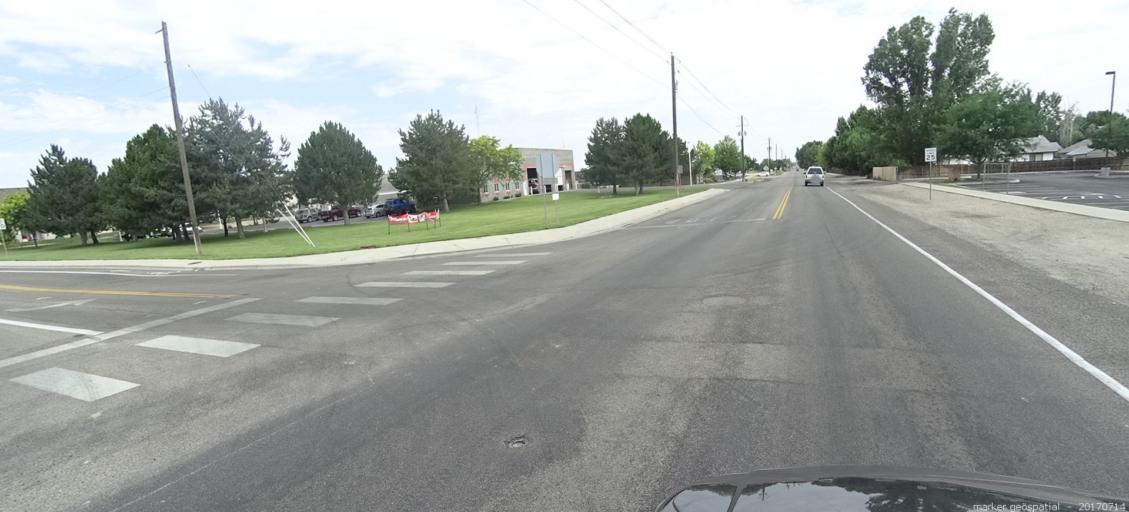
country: US
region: Idaho
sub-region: Ada County
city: Kuna
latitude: 43.4958
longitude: -116.4136
